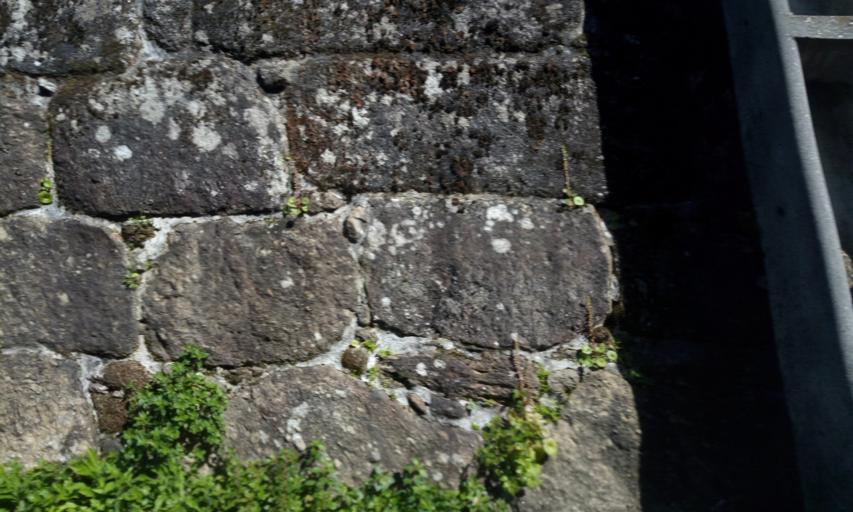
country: PT
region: Guarda
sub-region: Fornos de Algodres
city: Fornos de Algodres
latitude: 40.5170
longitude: -7.6099
